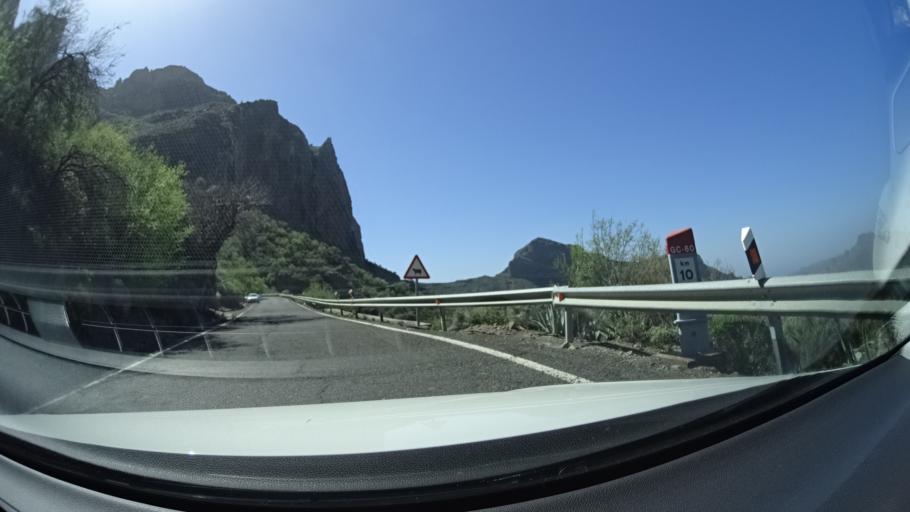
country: ES
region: Canary Islands
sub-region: Provincia de Las Palmas
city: Tejeda
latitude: 27.9717
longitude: -15.6200
